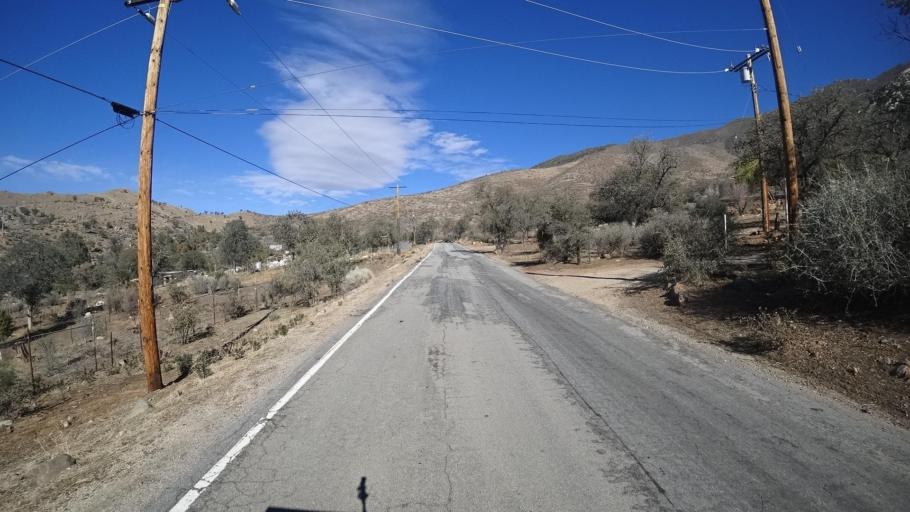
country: US
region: California
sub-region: Kern County
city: Bodfish
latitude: 35.5485
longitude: -118.5064
